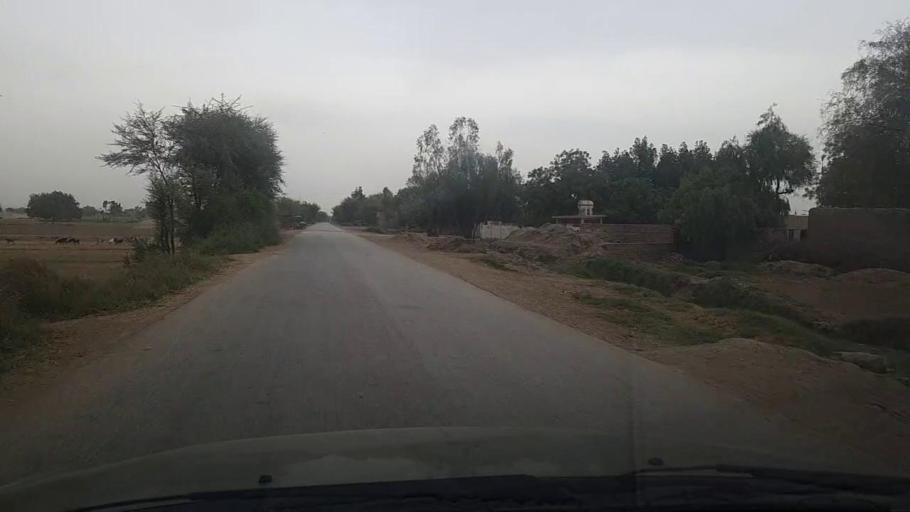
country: PK
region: Sindh
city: Daulatpur
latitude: 26.3228
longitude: 68.1070
